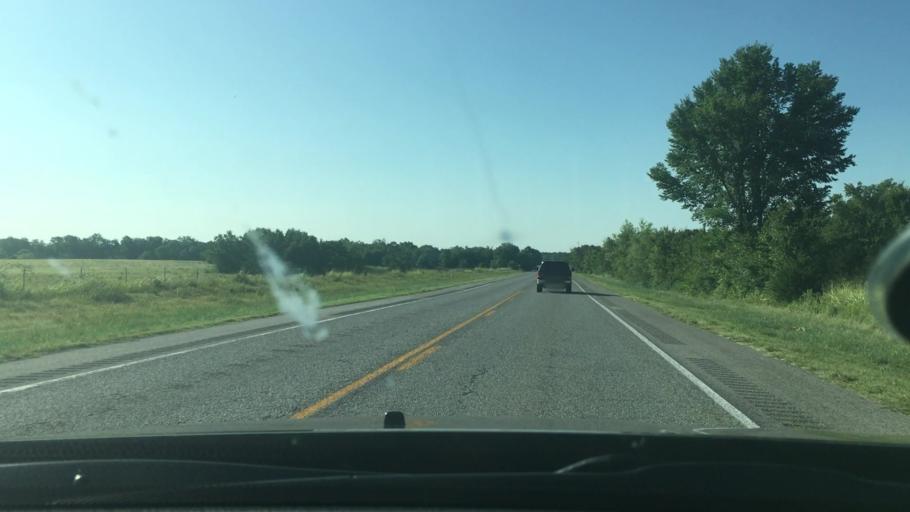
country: US
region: Oklahoma
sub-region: Johnston County
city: Tishomingo
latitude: 34.2555
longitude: -96.7645
